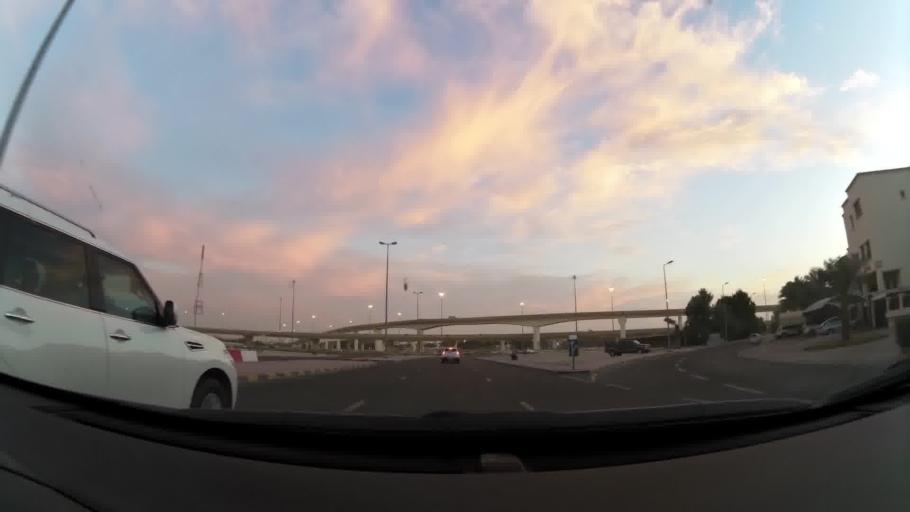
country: KW
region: Al Asimah
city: Ar Rabiyah
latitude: 29.3128
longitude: 47.8841
